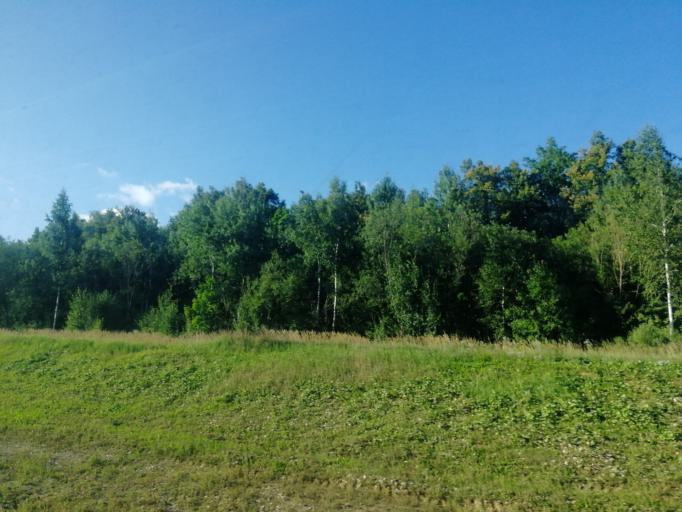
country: RU
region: Tula
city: Novogurovskiy
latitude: 54.2772
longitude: 37.2472
